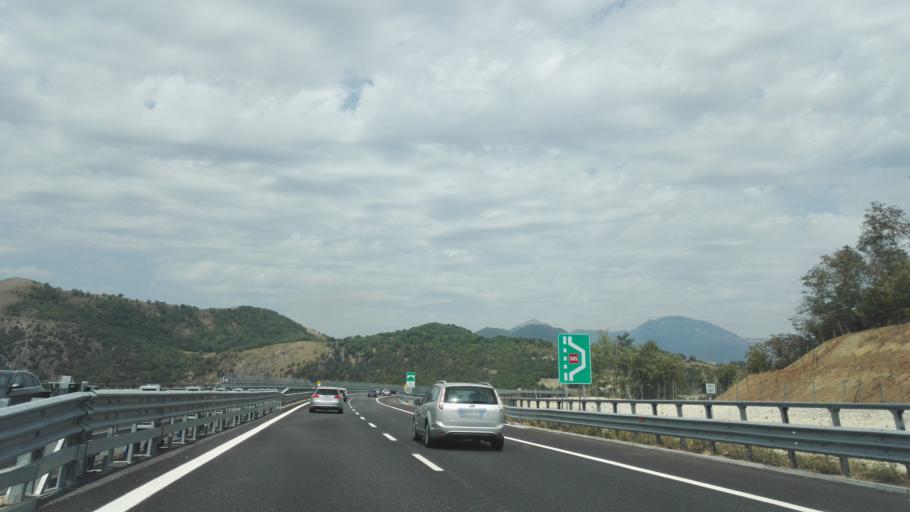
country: IT
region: Calabria
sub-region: Provincia di Cosenza
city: Laino Castello-Nuovo Centro
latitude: 39.9329
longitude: 15.9623
